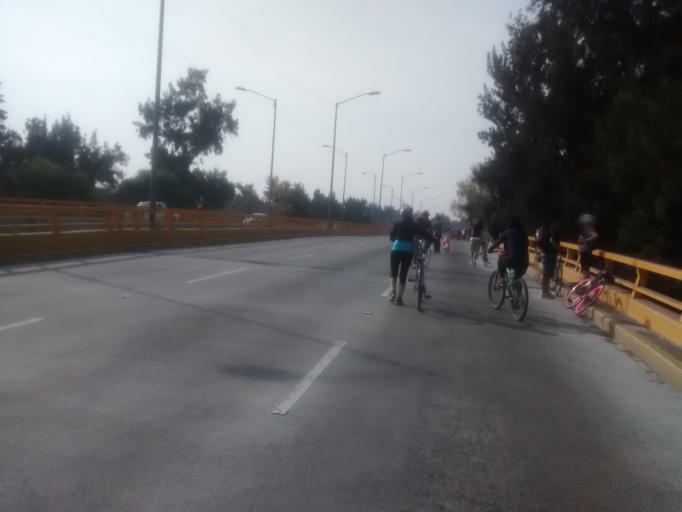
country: MX
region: Mexico City
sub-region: Iztacalco
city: Iztacalco
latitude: 19.3798
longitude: -99.1014
